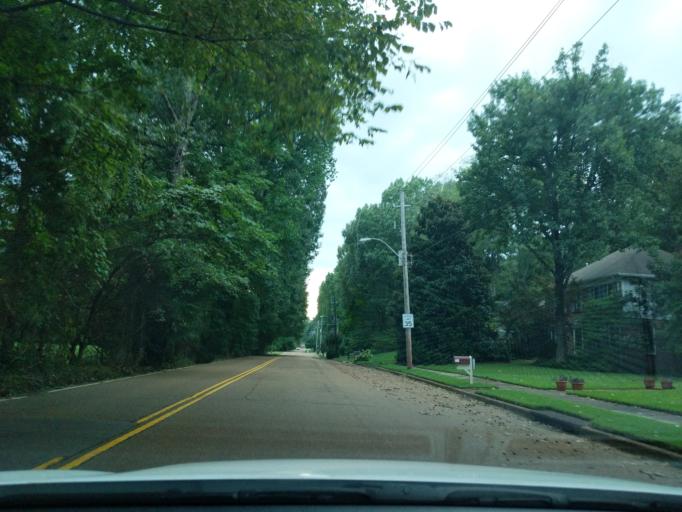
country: US
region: Tennessee
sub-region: Shelby County
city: Germantown
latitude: 35.0775
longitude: -89.8172
